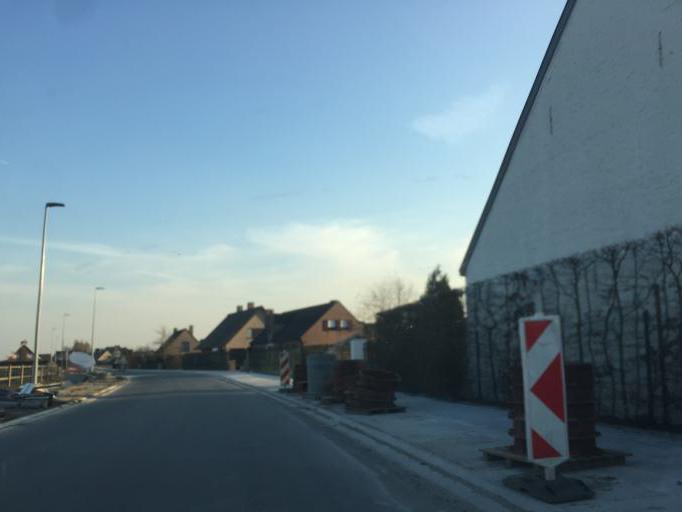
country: BE
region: Flanders
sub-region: Provincie West-Vlaanderen
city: Meulebeke
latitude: 50.9538
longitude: 3.3021
